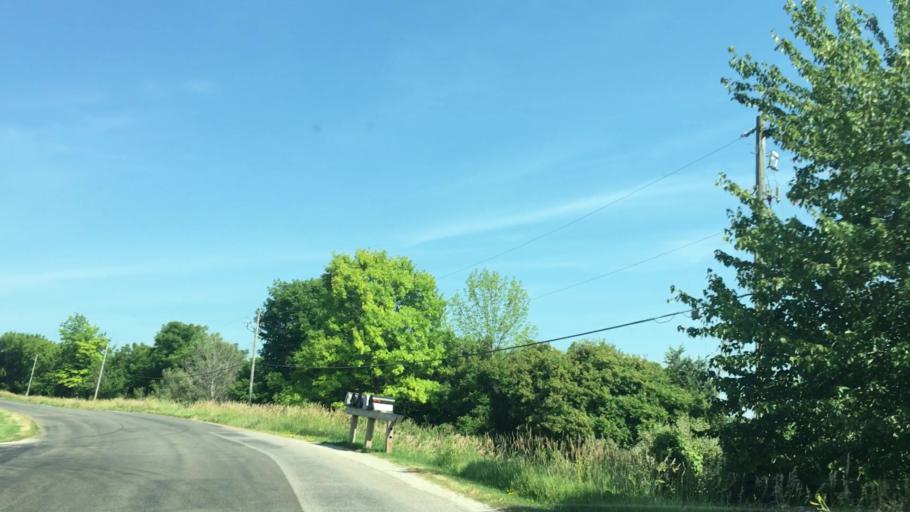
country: US
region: Iowa
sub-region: Johnson County
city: Iowa City
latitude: 41.6886
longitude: -91.5411
